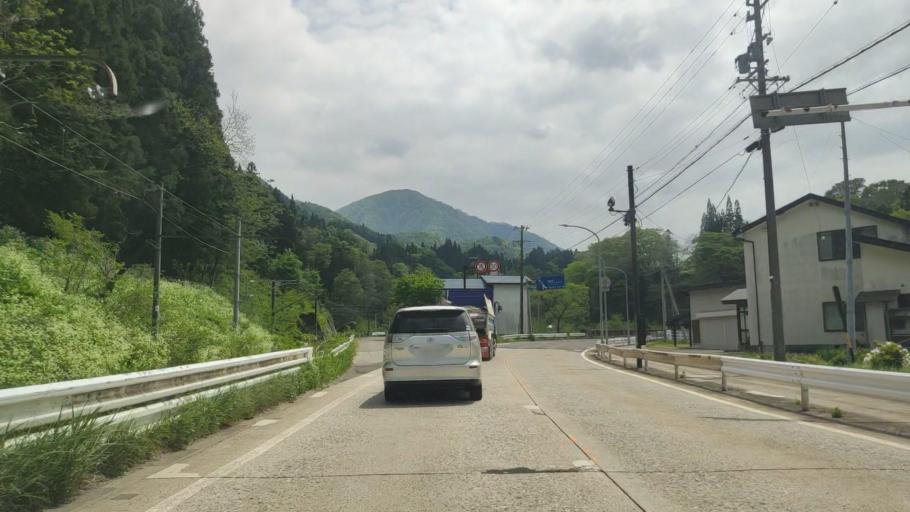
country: JP
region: Nagano
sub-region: Kitaazumi Gun
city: Hakuba
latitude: 36.7714
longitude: 137.9059
